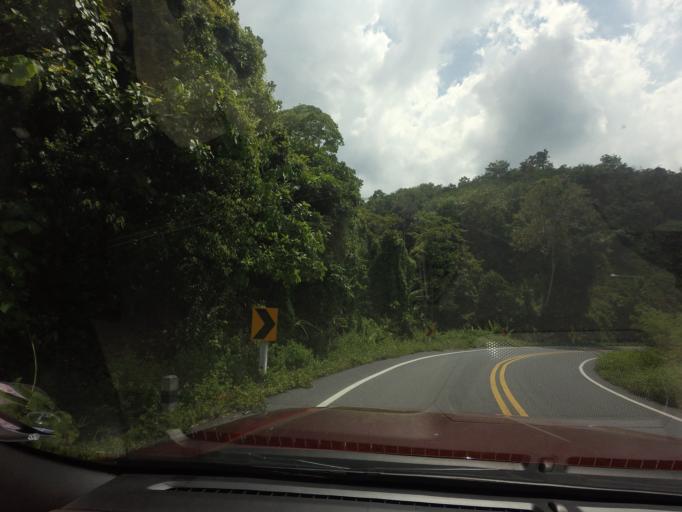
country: TH
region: Yala
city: Than To
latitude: 6.0343
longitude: 101.2072
